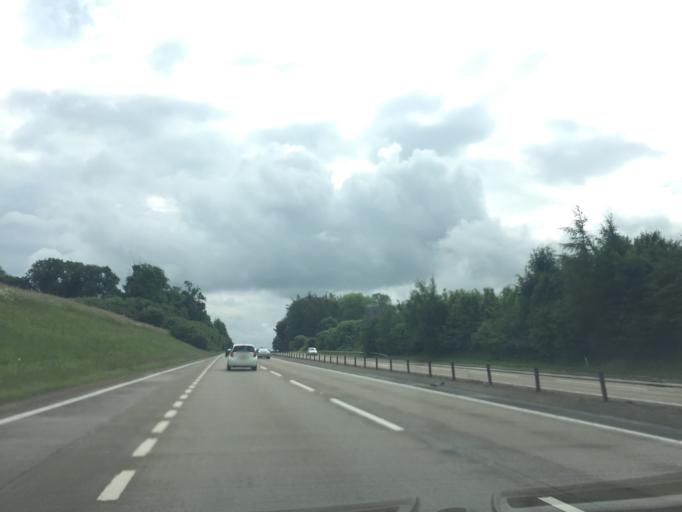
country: GB
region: England
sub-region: Dorset
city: Dorchester
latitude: 50.7544
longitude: -2.3373
